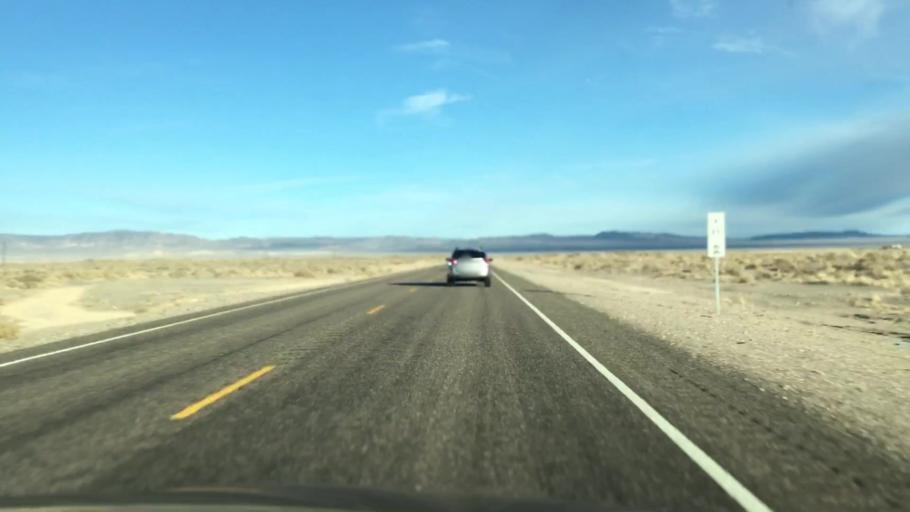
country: US
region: Nevada
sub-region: Nye County
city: Tonopah
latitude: 38.1402
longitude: -117.4868
